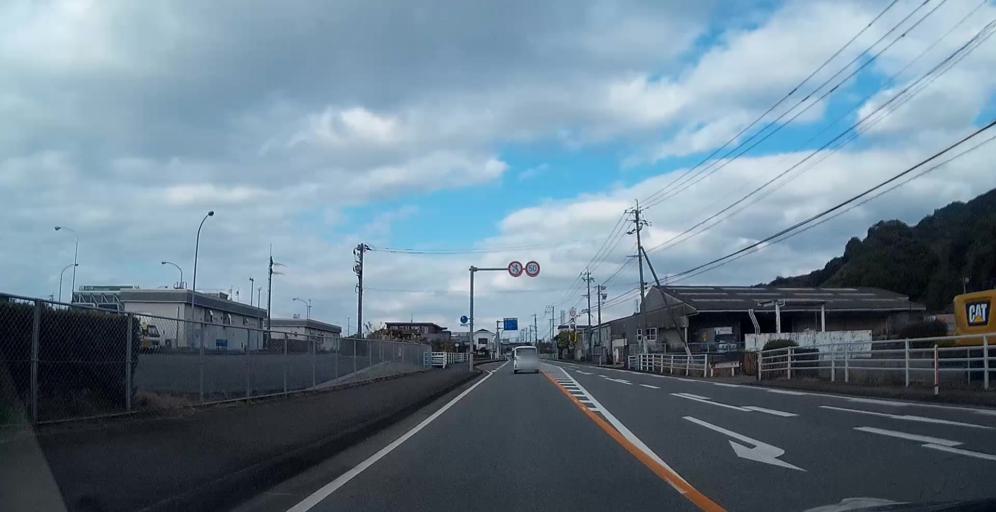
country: JP
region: Kumamoto
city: Yatsushiro
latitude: 32.4615
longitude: 130.6018
